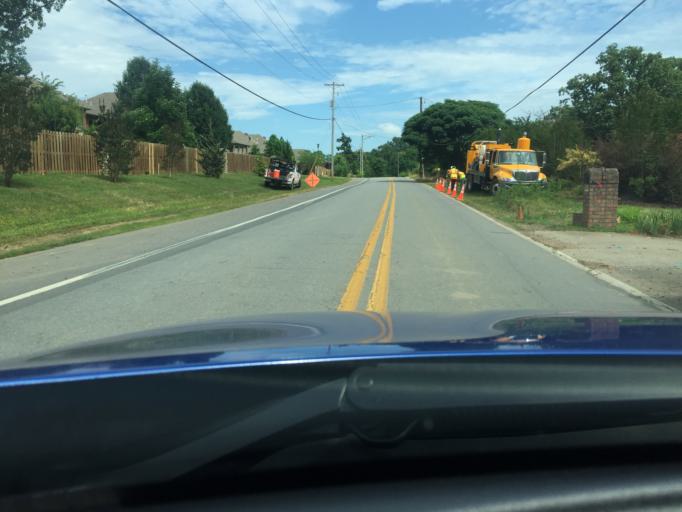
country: US
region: Arkansas
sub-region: Pulaski County
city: Maumelle
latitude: 34.8057
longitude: -92.4366
